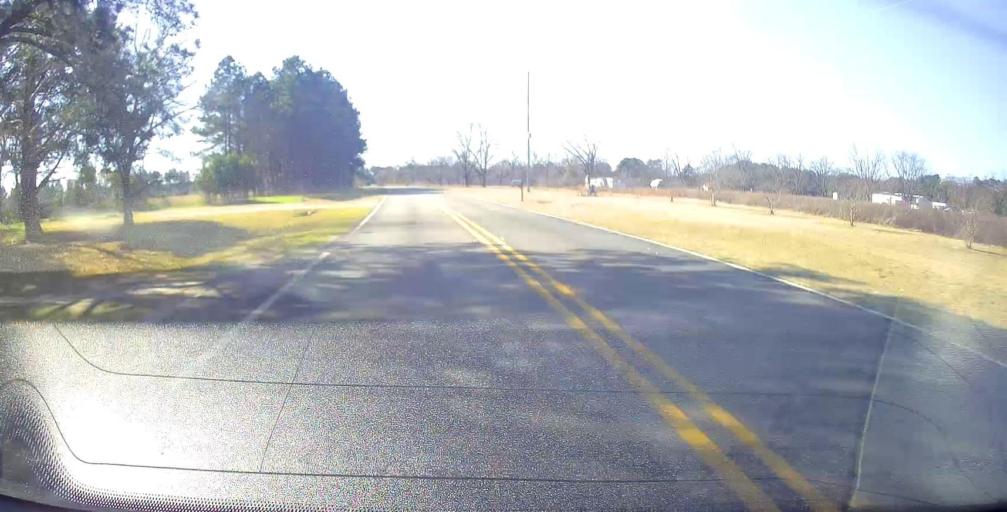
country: US
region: Georgia
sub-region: Macon County
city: Montezuma
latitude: 32.2787
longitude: -84.0055
